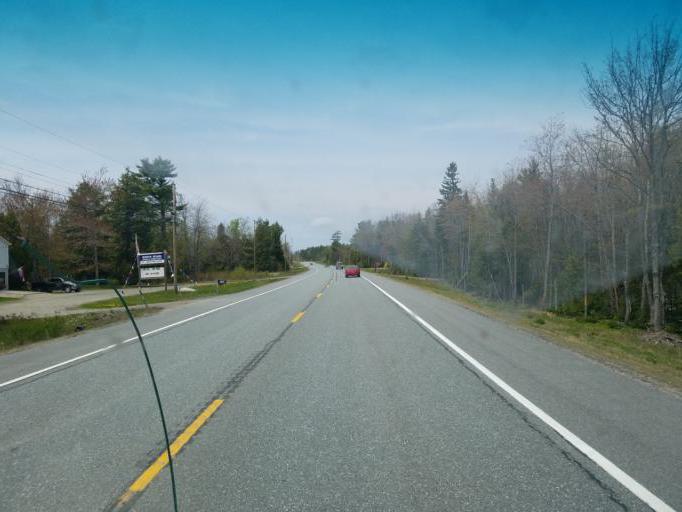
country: US
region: Maine
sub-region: Hancock County
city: Surry
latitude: 44.6072
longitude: -68.5184
